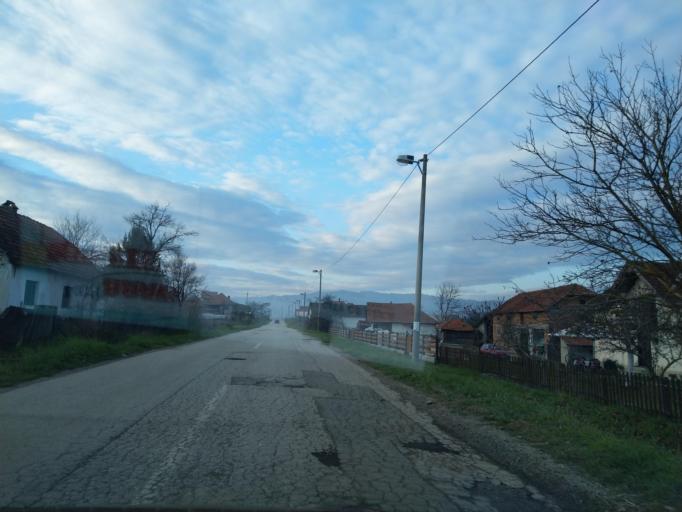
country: RS
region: Central Serbia
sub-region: Zlatiborski Okrug
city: Kosjeric
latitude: 43.9190
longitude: 19.9073
